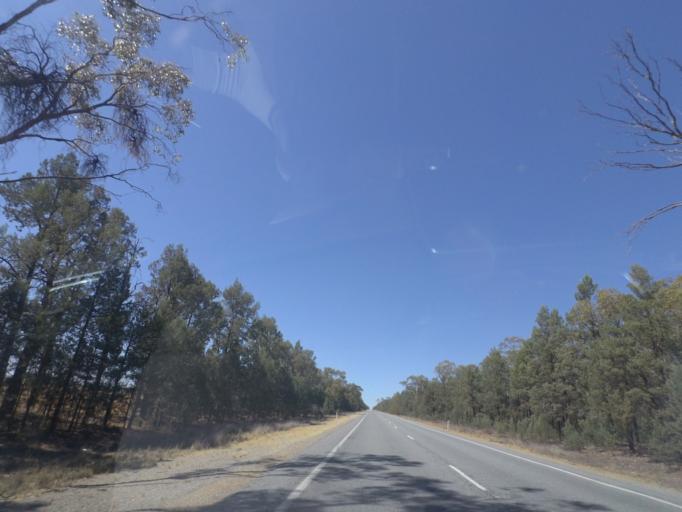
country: AU
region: New South Wales
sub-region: Narrandera
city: Narrandera
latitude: -34.4244
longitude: 146.8444
